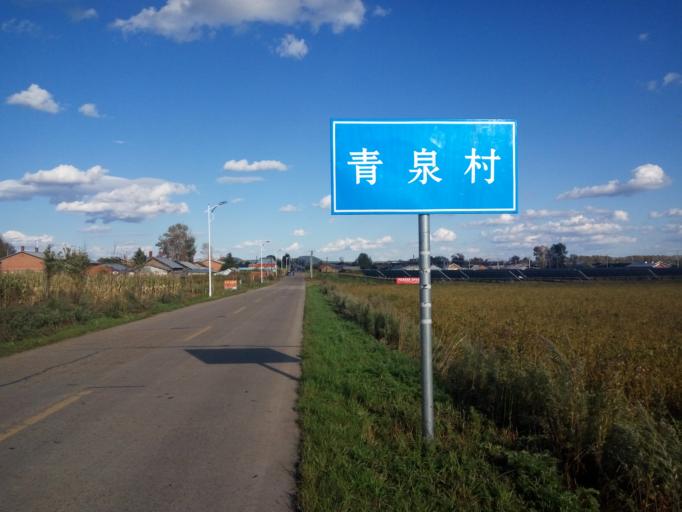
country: CN
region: Heilongjiang Sheng
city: Erjing
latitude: 48.6405
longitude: 126.1281
